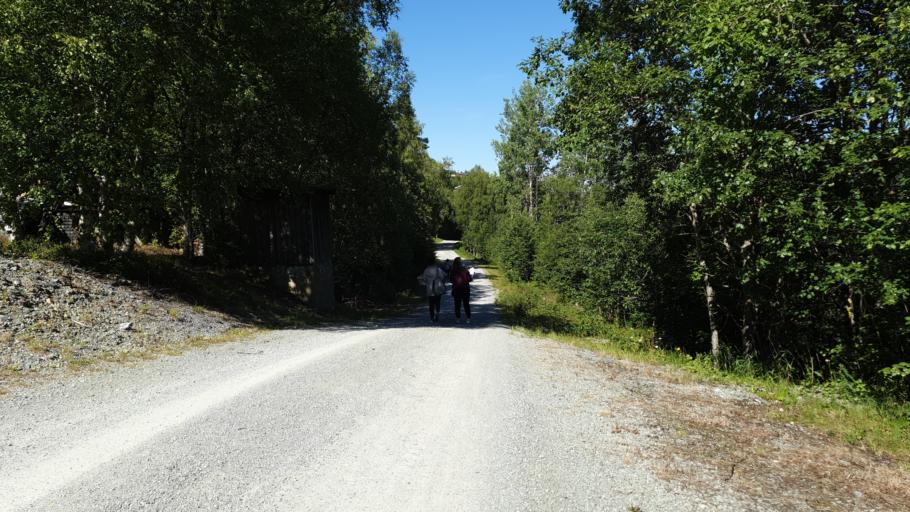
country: NO
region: Sor-Trondelag
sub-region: Meldal
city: Meldal
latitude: 63.1223
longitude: 9.7016
